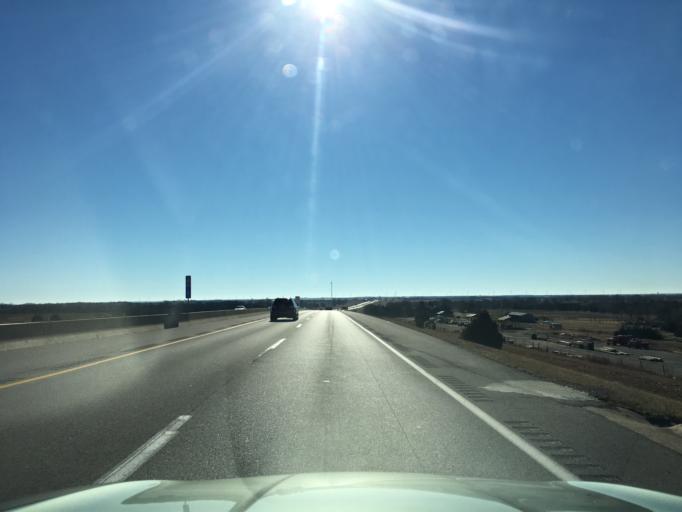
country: US
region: Kansas
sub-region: Sumner County
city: Wellington
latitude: 37.2653
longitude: -97.3400
